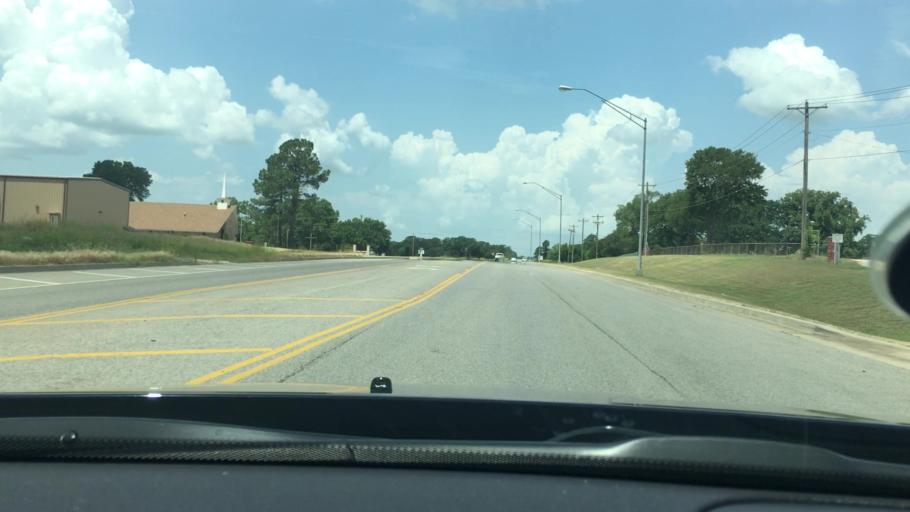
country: US
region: Oklahoma
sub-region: Marshall County
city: Oakland
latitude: 34.0998
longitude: -96.7820
